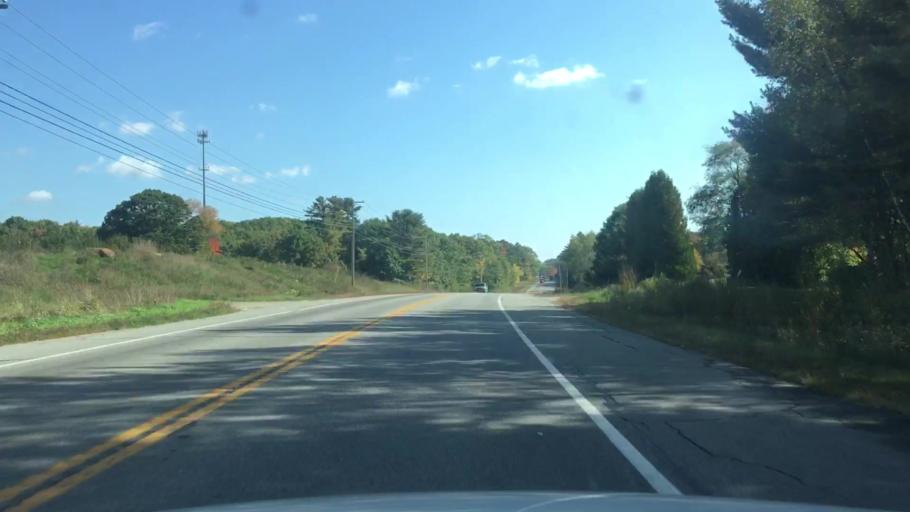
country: US
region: Maine
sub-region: Knox County
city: Warren
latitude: 44.1201
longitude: -69.2762
